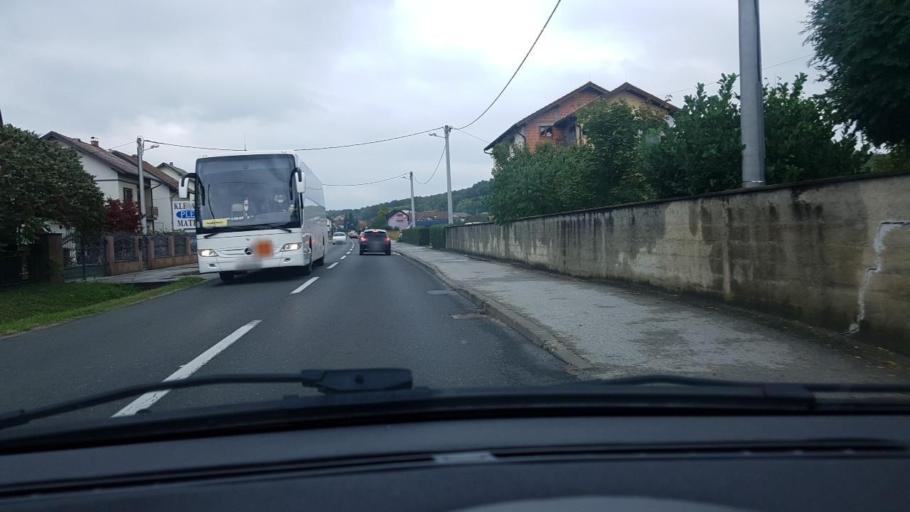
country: HR
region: Grad Zagreb
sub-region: Sesvete
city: Sesvete
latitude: 45.8576
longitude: 16.1135
